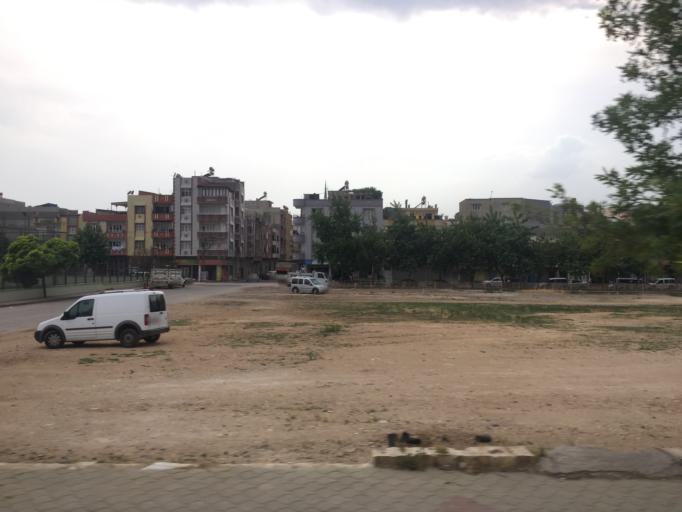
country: TR
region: Gaziantep
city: Gaziantep
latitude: 37.0658
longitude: 37.4147
